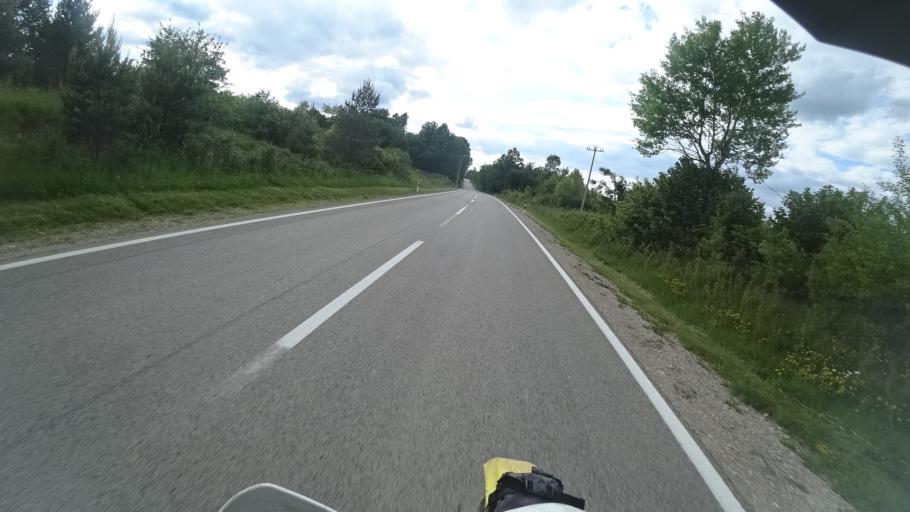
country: HR
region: Licko-Senjska
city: Gospic
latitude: 44.5067
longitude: 15.4430
